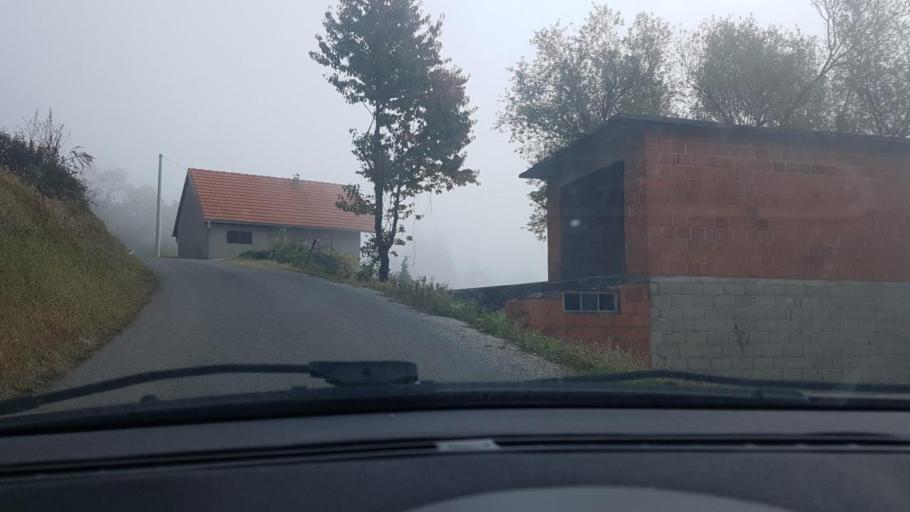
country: HR
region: Krapinsko-Zagorska
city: Mihovljan
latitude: 46.1598
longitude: 15.9957
